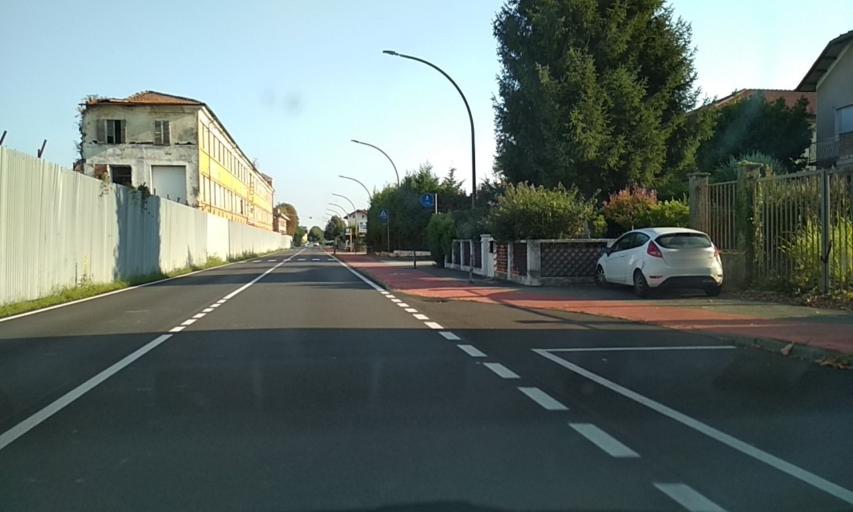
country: IT
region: Piedmont
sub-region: Provincia di Torino
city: Rivarolo Canavese
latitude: 45.3239
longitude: 7.7279
